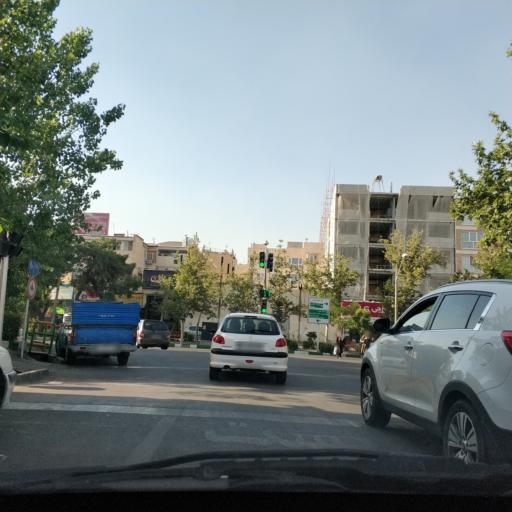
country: IR
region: Tehran
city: Tehran
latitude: 35.7205
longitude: 51.4853
